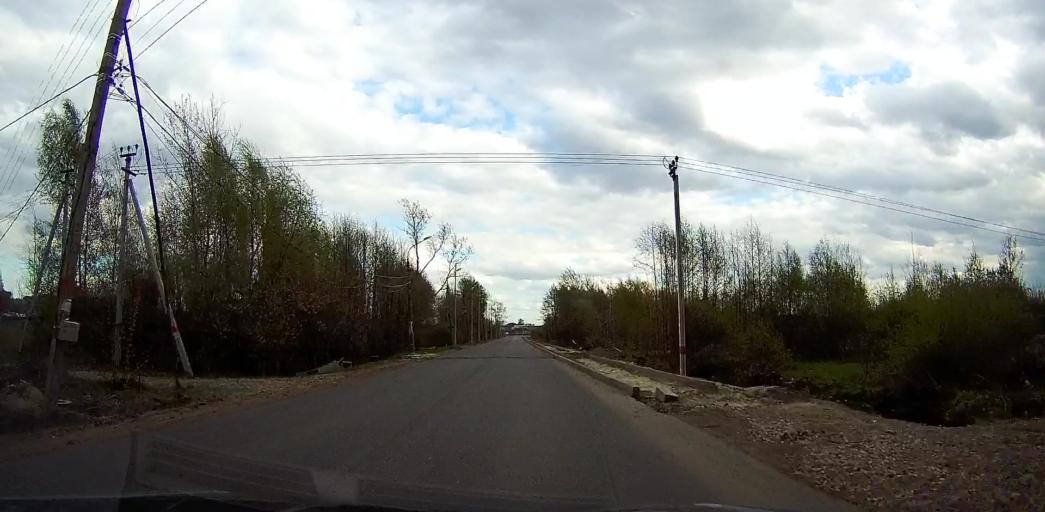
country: RU
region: Moskovskaya
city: Pavlovskiy Posad
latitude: 55.7995
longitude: 38.6863
